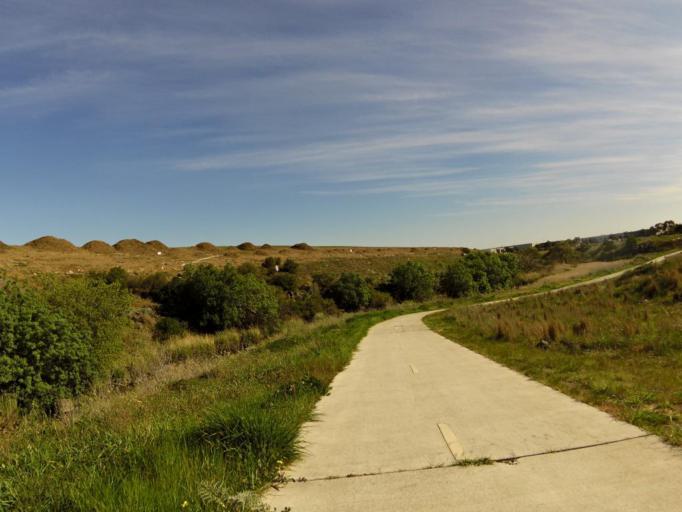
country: AU
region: Victoria
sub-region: Brimbank
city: Brooklyn
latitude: -37.8099
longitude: 144.8308
